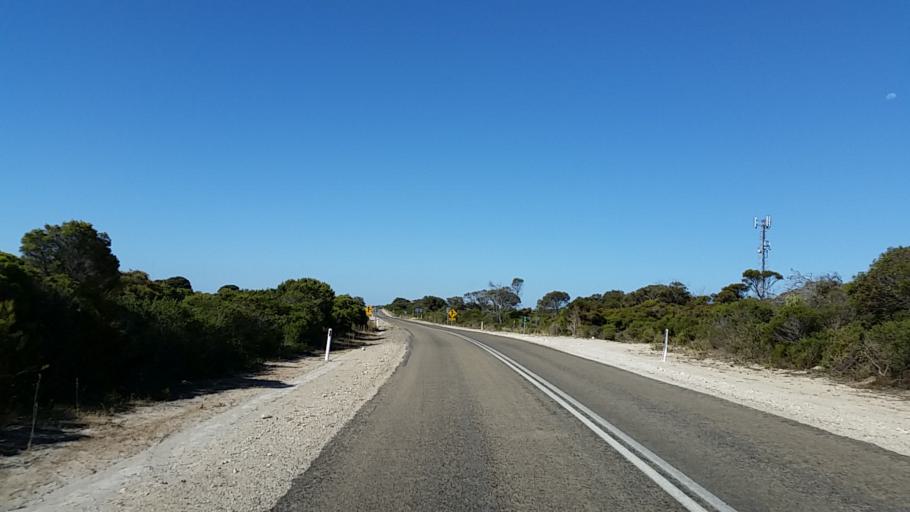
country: AU
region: South Australia
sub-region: Yorke Peninsula
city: Honiton
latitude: -35.2454
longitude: 136.9729
